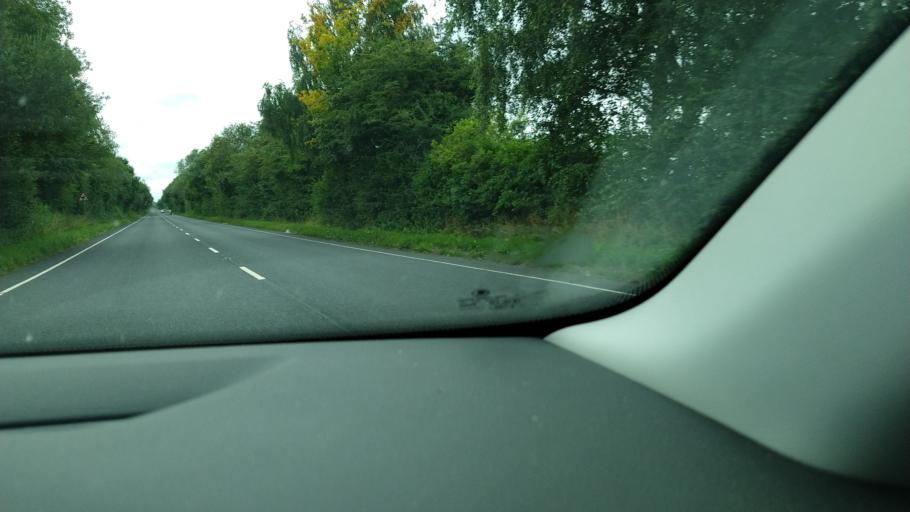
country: GB
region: England
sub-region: East Riding of Yorkshire
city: Barmby on the Marsh
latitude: 53.7173
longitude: -0.9665
